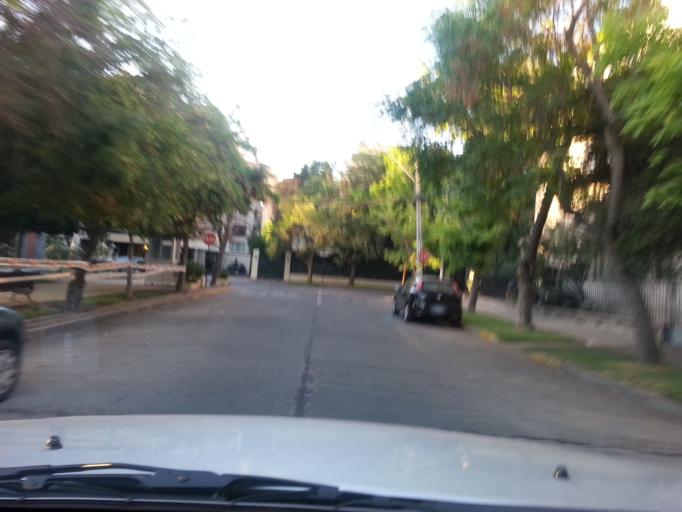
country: CL
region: Santiago Metropolitan
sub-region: Provincia de Santiago
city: Villa Presidente Frei, Nunoa, Santiago, Chile
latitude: -33.4264
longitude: -70.5946
